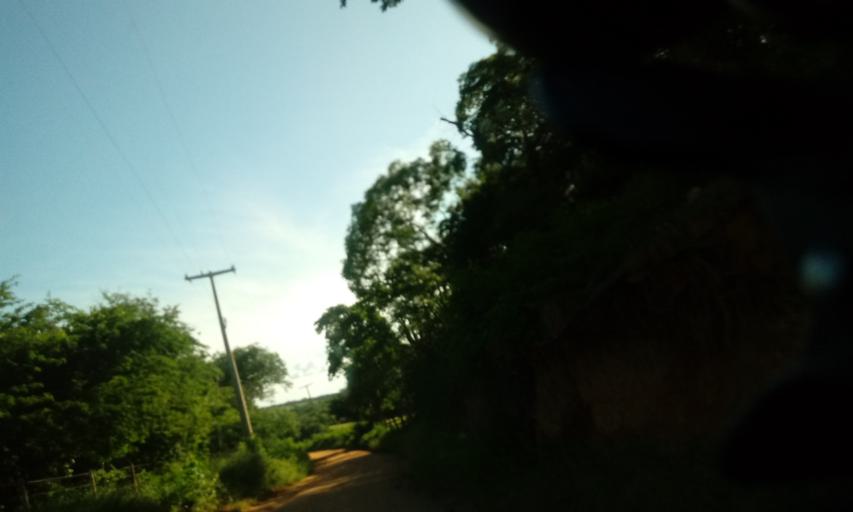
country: BR
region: Bahia
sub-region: Riacho De Santana
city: Riacho de Santana
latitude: -13.8289
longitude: -42.7672
